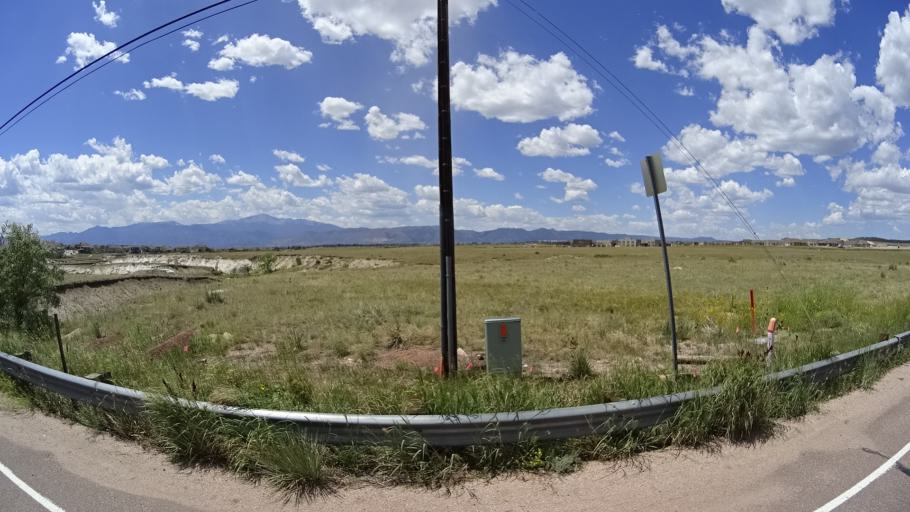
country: US
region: Colorado
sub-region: El Paso County
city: Black Forest
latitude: 38.9559
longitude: -104.7007
